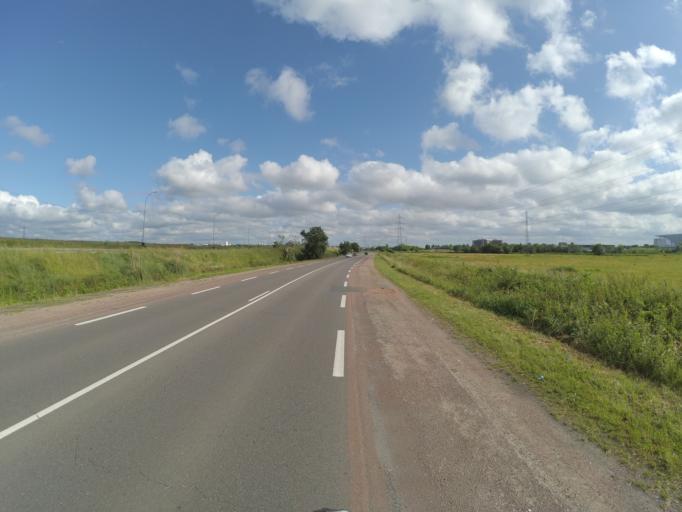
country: FR
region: Aquitaine
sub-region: Departement de la Gironde
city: Bassens
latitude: 44.9027
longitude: -0.5535
